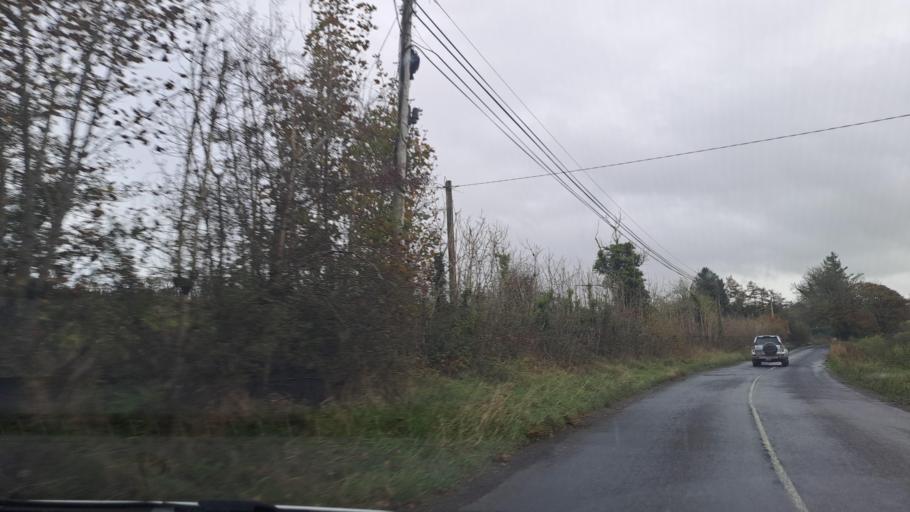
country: IE
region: Ulster
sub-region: An Cabhan
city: Bailieborough
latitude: 53.9556
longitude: -7.0335
